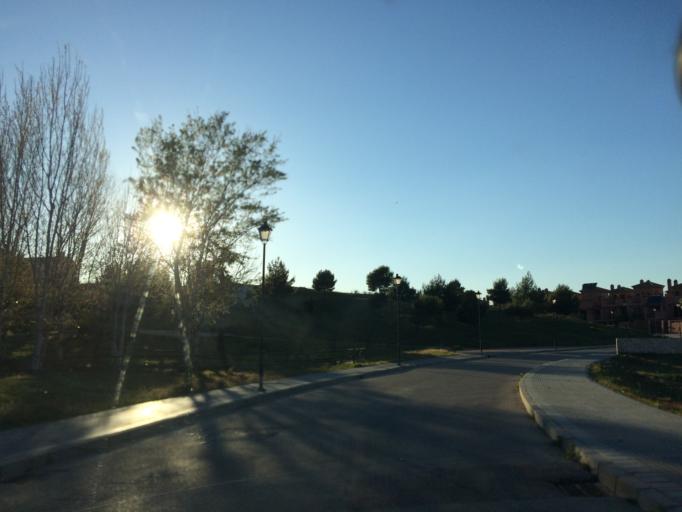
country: ES
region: Andalusia
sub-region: Provincia de Malaga
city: Alhaurin de la Torre
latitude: 36.6642
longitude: -4.5370
